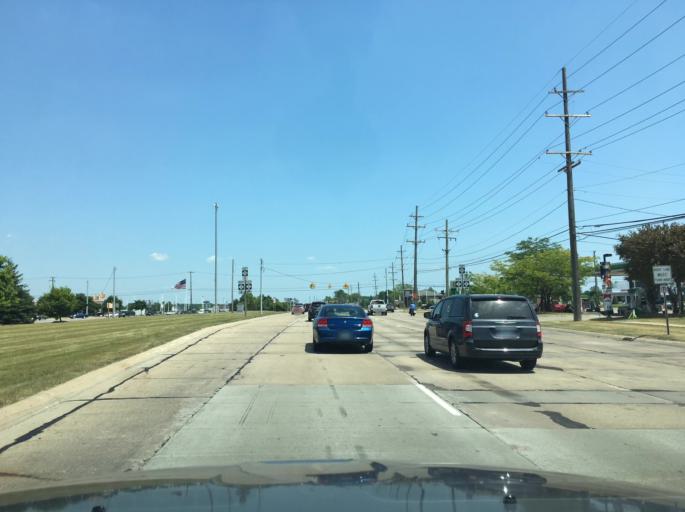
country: US
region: Michigan
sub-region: Macomb County
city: Mount Clemens
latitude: 42.6299
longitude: -82.8626
